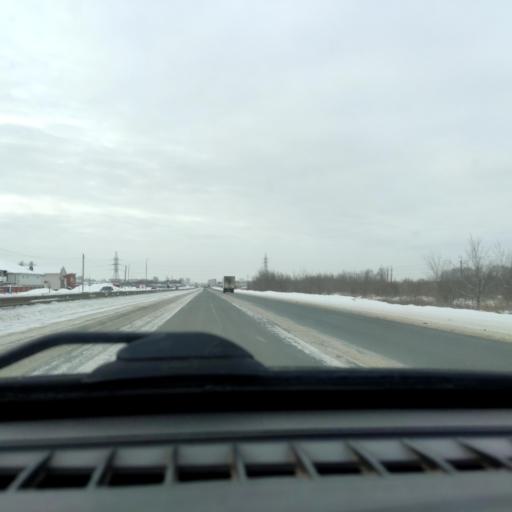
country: RU
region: Samara
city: Tol'yatti
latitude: 53.5656
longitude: 49.3676
